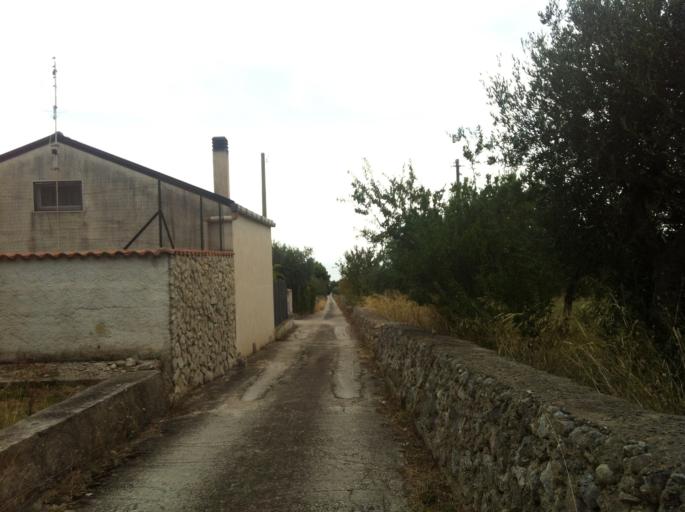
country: IT
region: Apulia
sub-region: Provincia di Foggia
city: Monte Sant'Angelo
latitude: 41.6637
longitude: 15.9527
